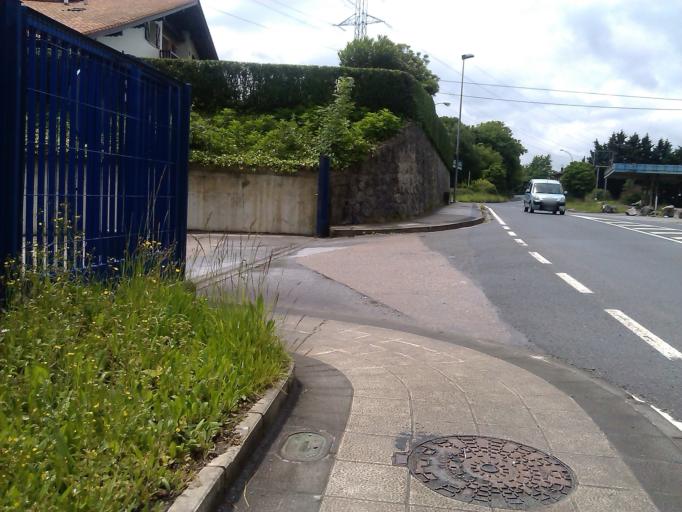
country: ES
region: Basque Country
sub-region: Provincia de Guipuzcoa
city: Urnieta
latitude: 43.2384
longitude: -1.9972
